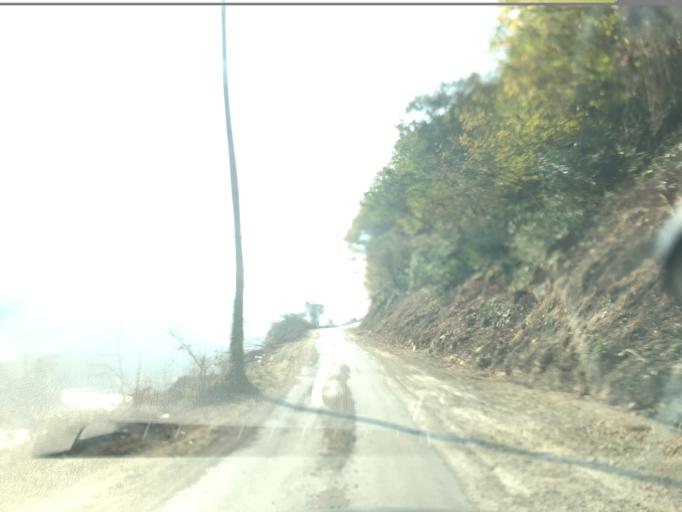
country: TR
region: Duzce
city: Cumayeri
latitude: 40.9267
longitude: 30.9299
